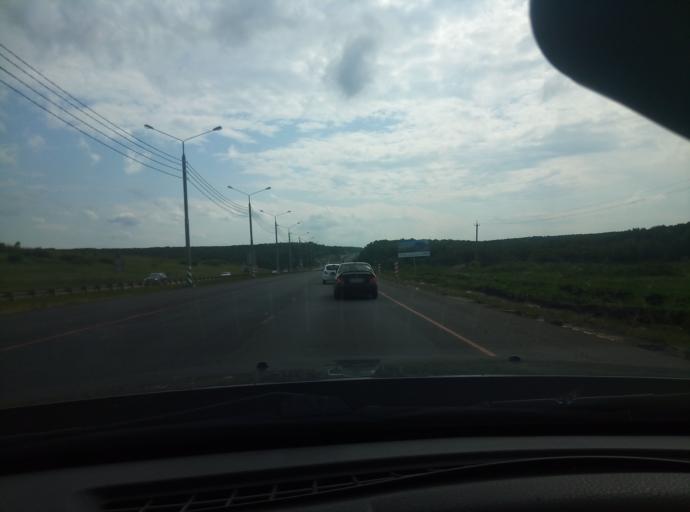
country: RU
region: Tula
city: Leninskiy
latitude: 54.4249
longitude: 37.5044
